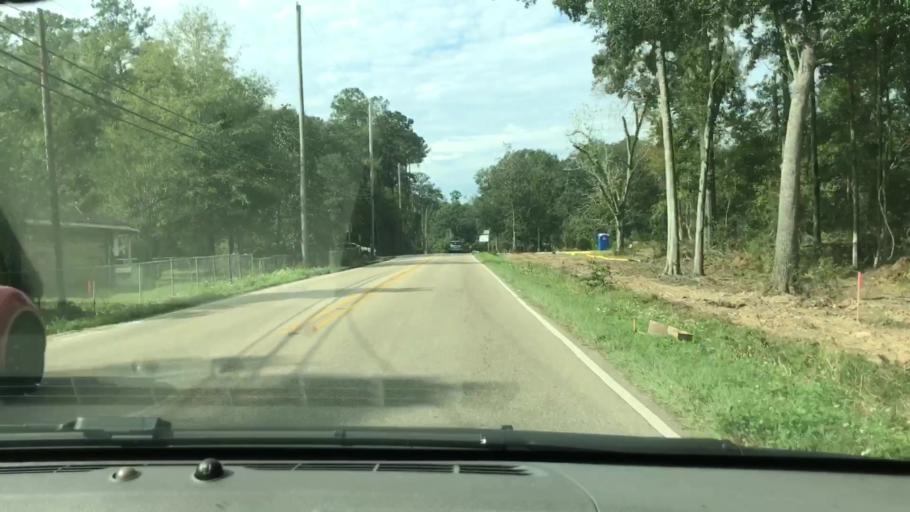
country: US
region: Louisiana
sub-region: Saint Tammany Parish
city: Covington
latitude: 30.4598
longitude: -90.0722
